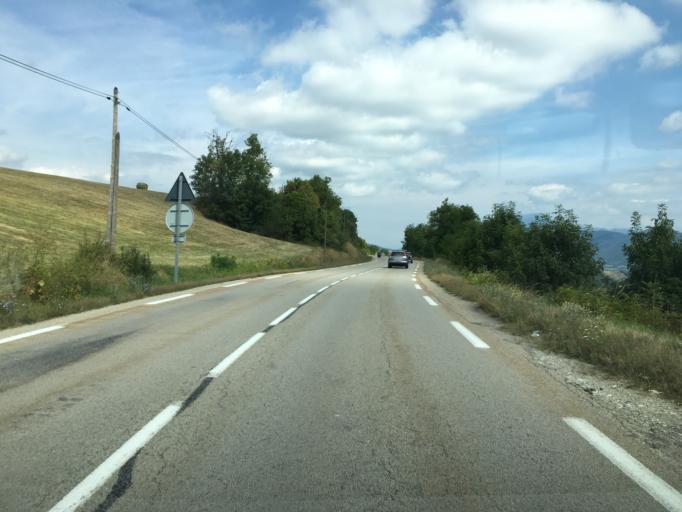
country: FR
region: Rhone-Alpes
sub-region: Departement de l'Isere
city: Mens
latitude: 44.7762
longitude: 5.6526
